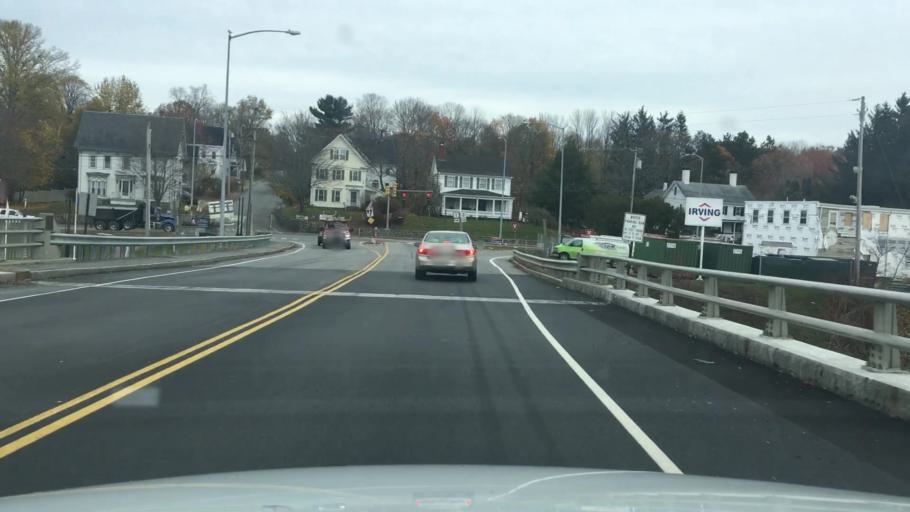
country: US
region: Maine
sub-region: Hancock County
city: Bucksport
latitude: 44.5702
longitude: -68.7878
